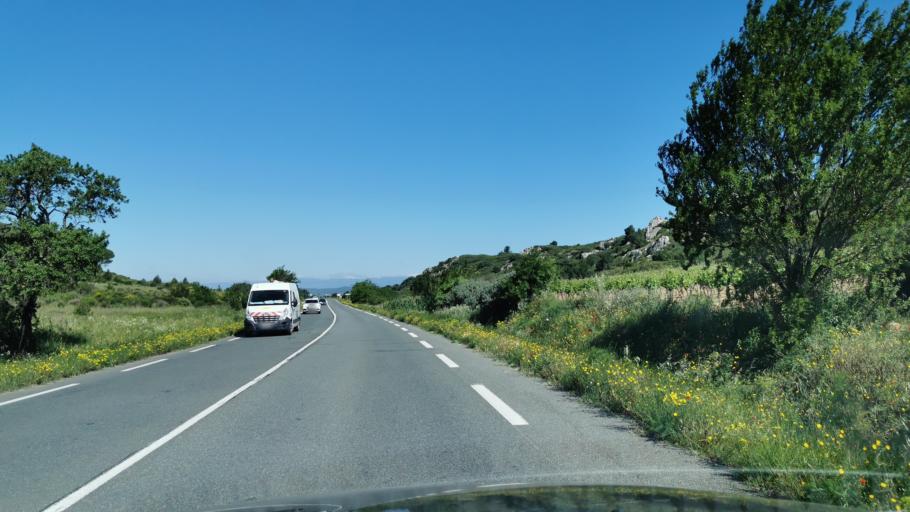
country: FR
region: Languedoc-Roussillon
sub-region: Departement de l'Aude
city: Nevian
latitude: 43.2048
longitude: 2.8879
